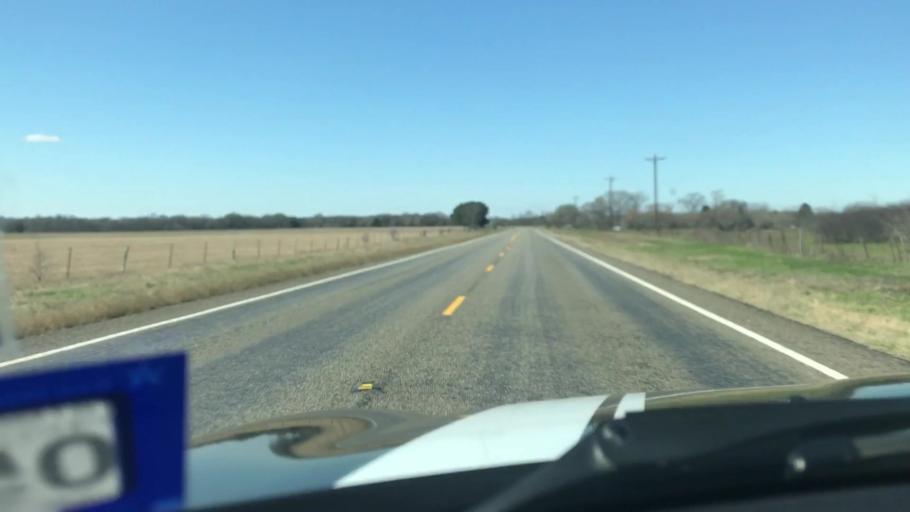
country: US
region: Texas
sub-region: Robertson County
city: Calvert
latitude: 30.8864
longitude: -96.8050
